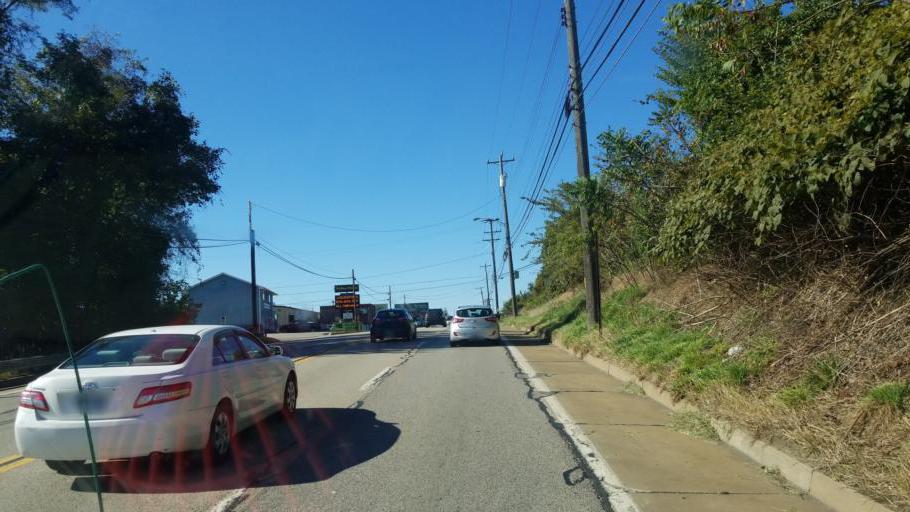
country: US
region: Pennsylvania
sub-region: Allegheny County
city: East McKeesport
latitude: 40.3722
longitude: -79.7907
